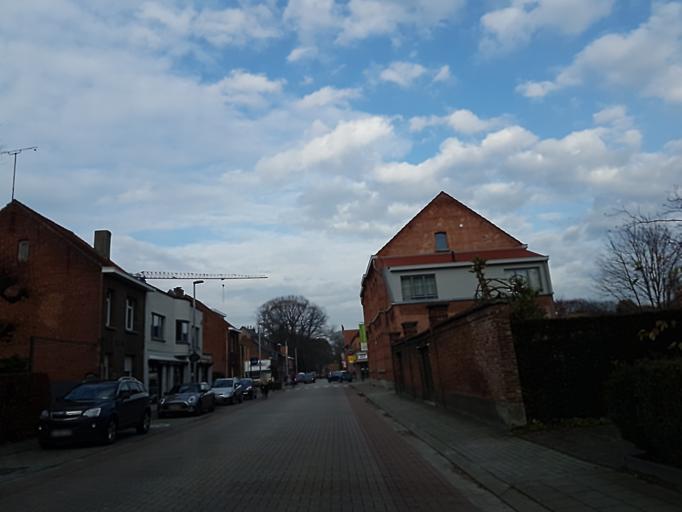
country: BE
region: Flanders
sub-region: Provincie Antwerpen
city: Kalmthout
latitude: 51.3839
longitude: 4.4752
